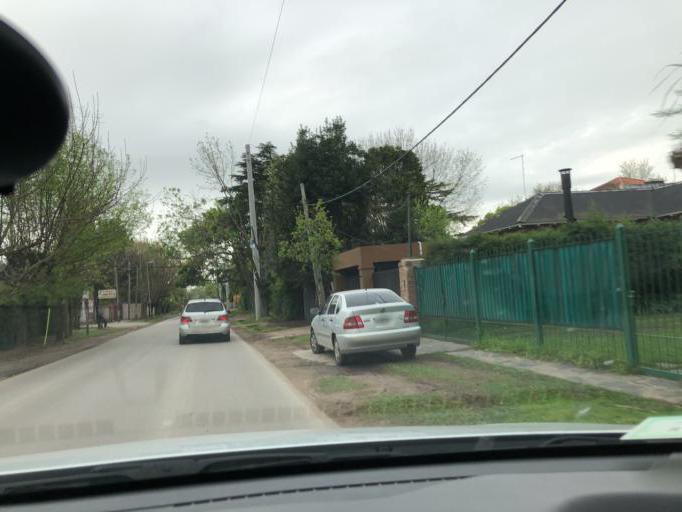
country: AR
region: Buenos Aires
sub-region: Partido de La Plata
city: La Plata
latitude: -34.8929
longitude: -58.0648
